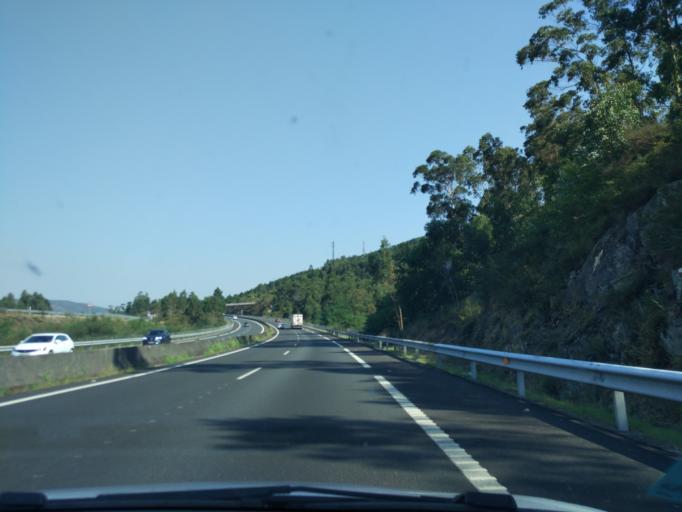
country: ES
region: Galicia
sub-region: Provincia da Coruna
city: Padron
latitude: 42.7458
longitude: -8.6439
